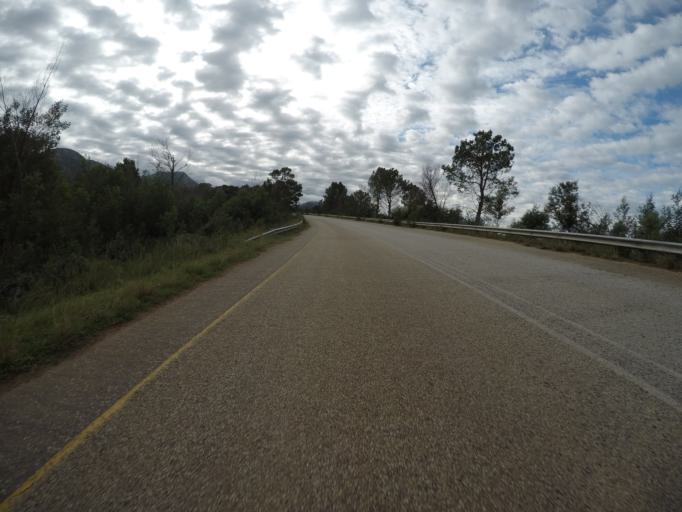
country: ZA
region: Eastern Cape
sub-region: Cacadu District Municipality
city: Kareedouw
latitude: -34.0151
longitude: 24.3040
